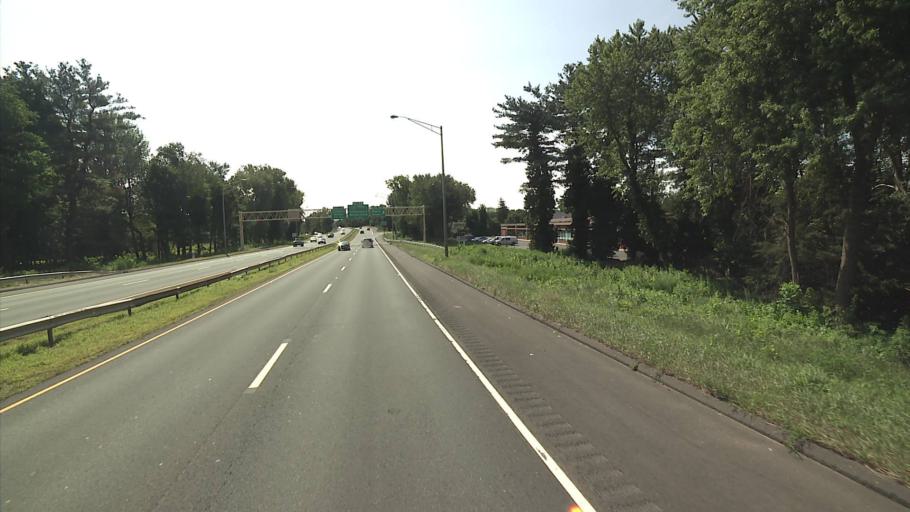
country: US
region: Connecticut
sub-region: Hartford County
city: Glastonbury
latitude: 41.7352
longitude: -72.6259
